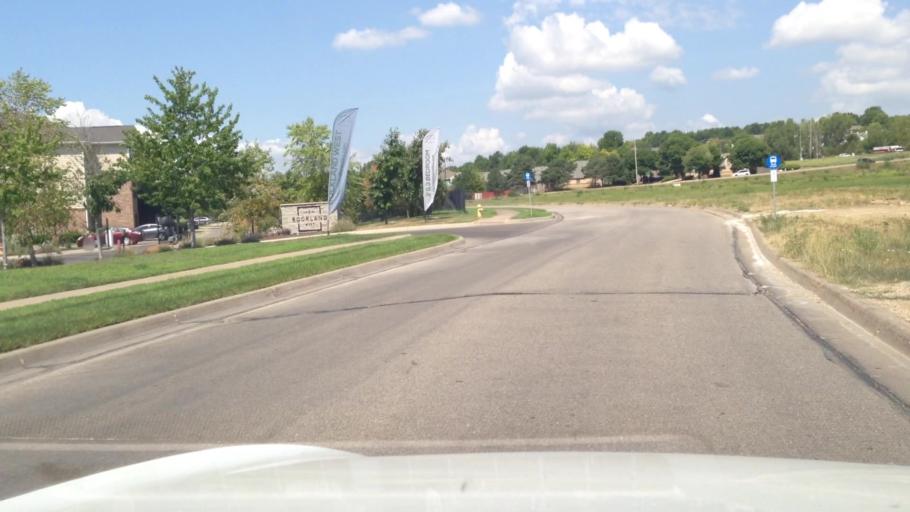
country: US
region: Kansas
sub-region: Douglas County
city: Lawrence
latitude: 38.9408
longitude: -95.2954
